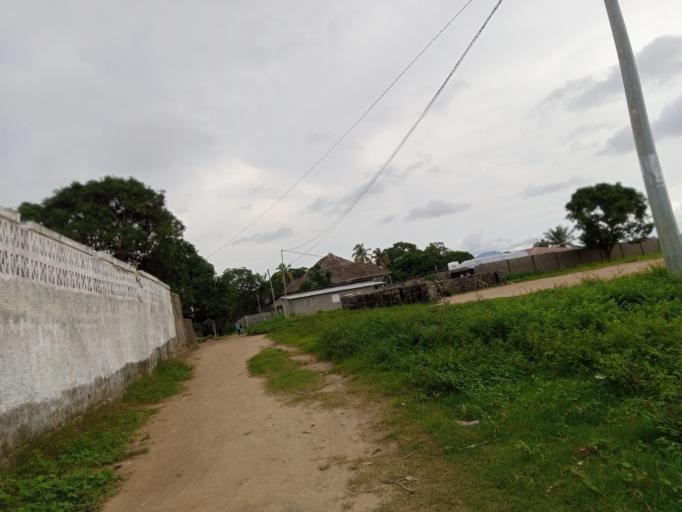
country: SL
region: Northern Province
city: Masoyila
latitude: 8.6004
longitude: -13.2030
